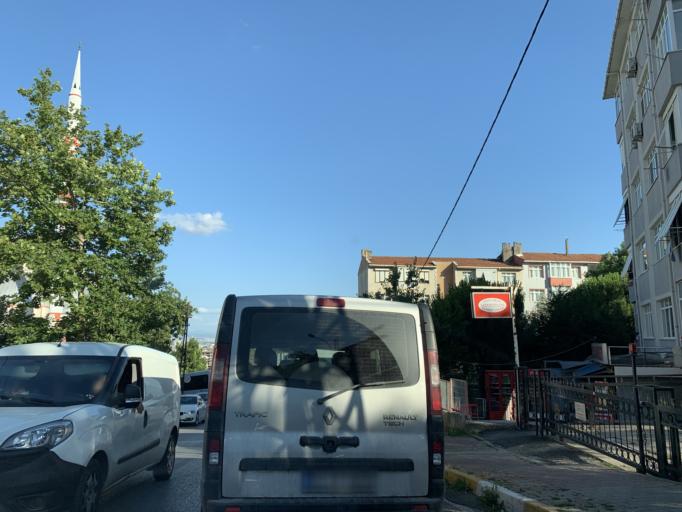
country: TR
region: Istanbul
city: Pendik
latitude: 40.8985
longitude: 29.2491
